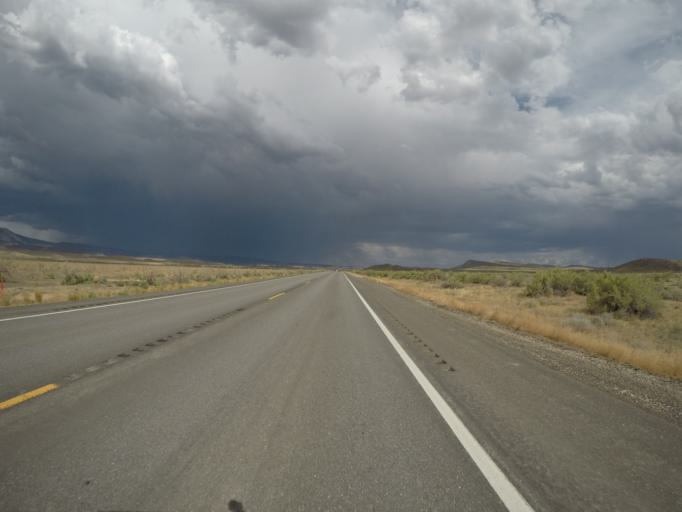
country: US
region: Utah
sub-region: Uintah County
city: Naples
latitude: 40.2920
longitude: -109.1699
